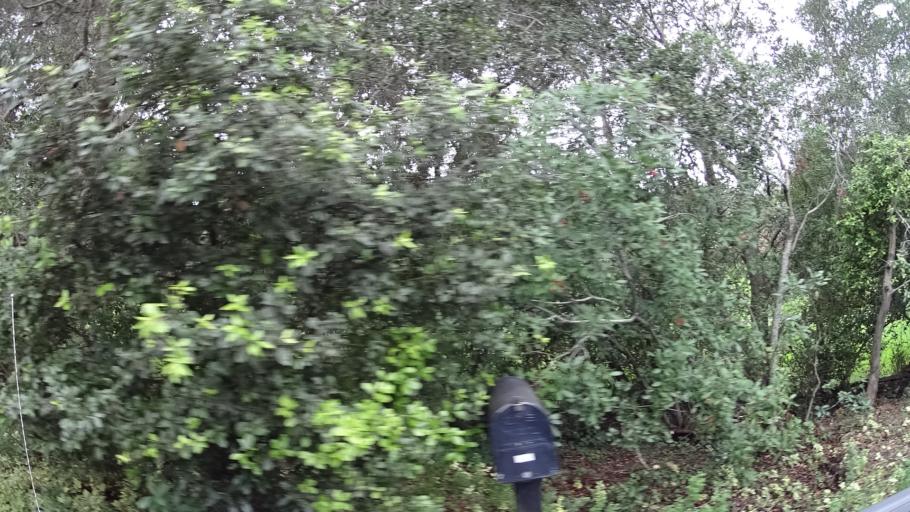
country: US
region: California
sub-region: San Mateo County
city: Hillsborough
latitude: 37.5669
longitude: -122.3664
